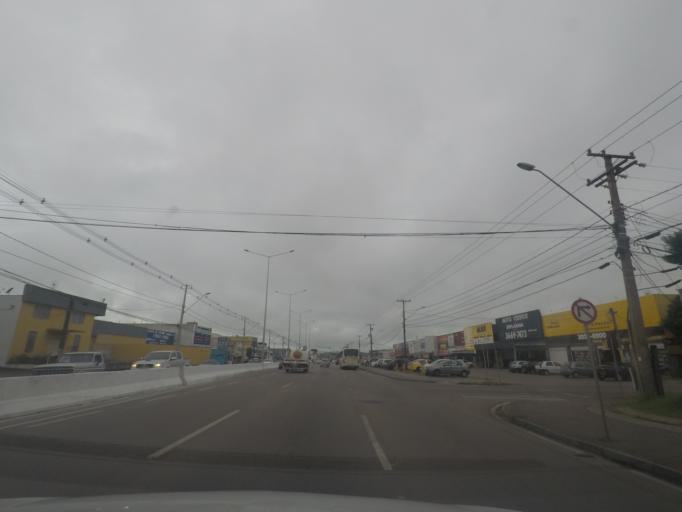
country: BR
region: Parana
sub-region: Pinhais
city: Pinhais
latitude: -25.4342
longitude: -49.1766
